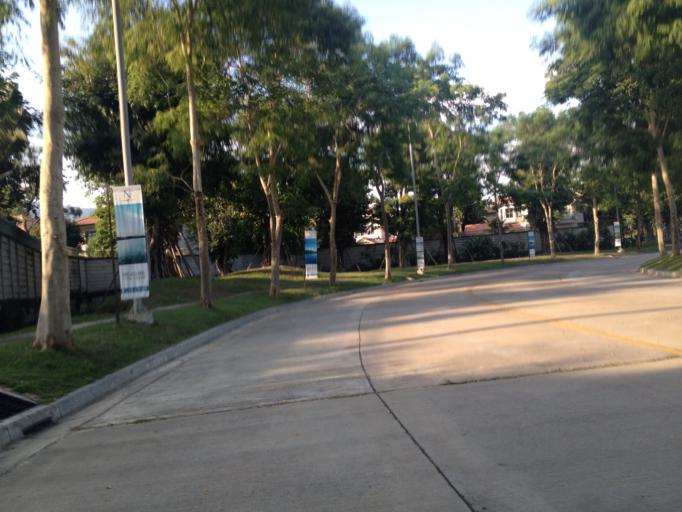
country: TH
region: Chiang Mai
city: Chiang Mai
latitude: 18.7544
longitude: 98.9481
